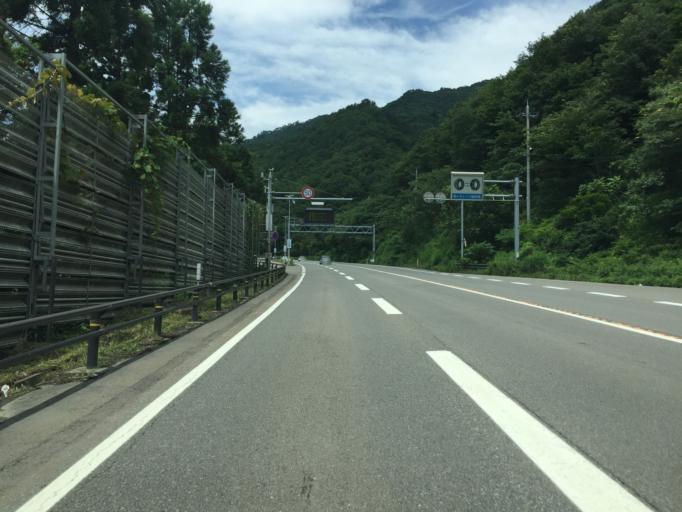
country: JP
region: Fukushima
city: Fukushima-shi
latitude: 37.8411
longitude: 140.3120
